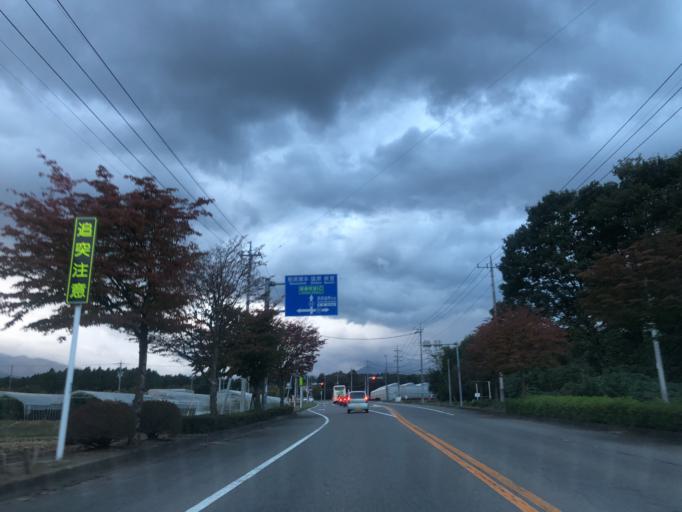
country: JP
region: Tochigi
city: Kuroiso
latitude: 36.9534
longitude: 140.0038
